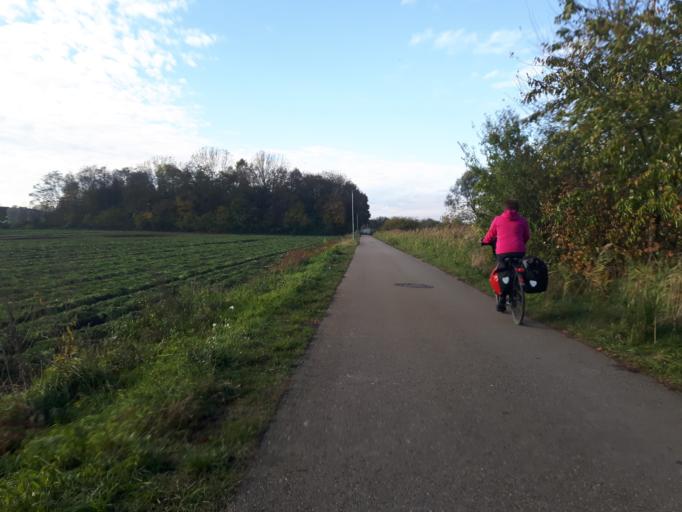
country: DE
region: Baden-Wuerttemberg
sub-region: Karlsruhe Region
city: Sankt Leon-Rot
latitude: 49.2621
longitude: 8.6175
